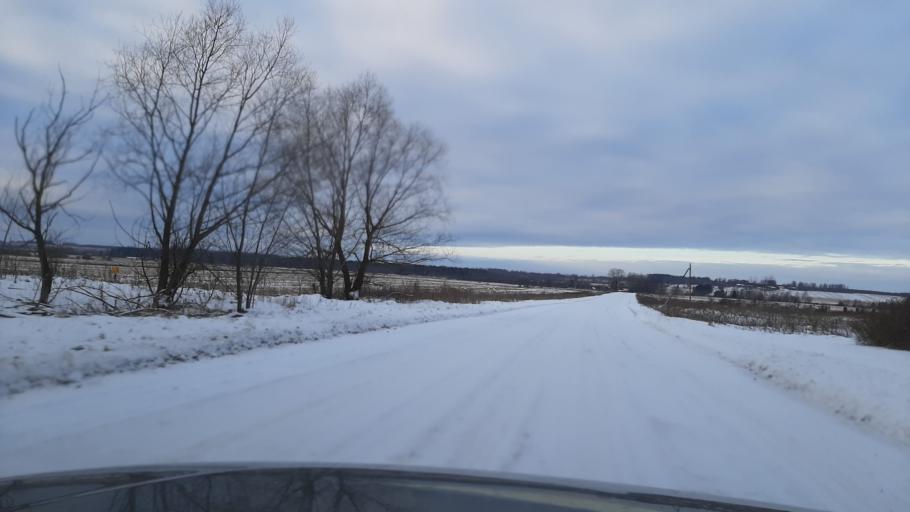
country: RU
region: Kostroma
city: Kosmynino
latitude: 57.4831
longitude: 40.8059
